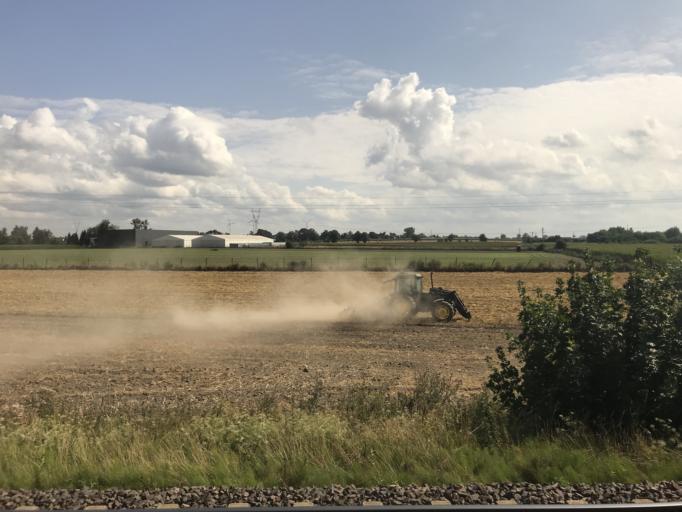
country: PL
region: Kujawsko-Pomorskie
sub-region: Powiat inowroclawski
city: Zlotniki Kujawskie
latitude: 52.9140
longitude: 18.1361
